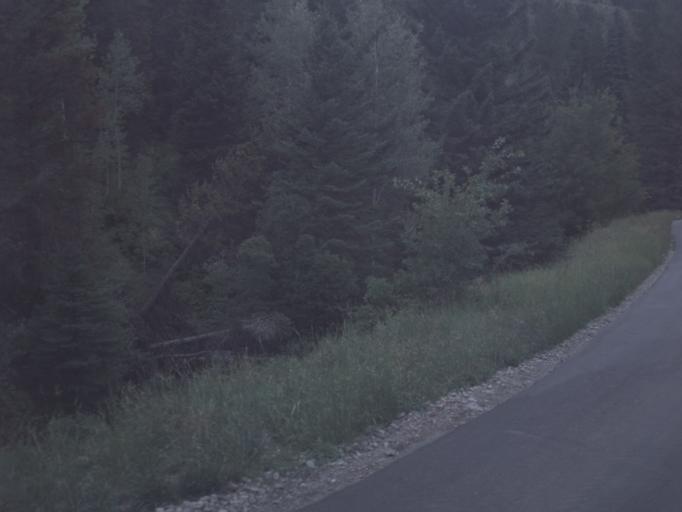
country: US
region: Utah
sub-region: Utah County
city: Cedar Hills
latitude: 40.4367
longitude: -111.6352
